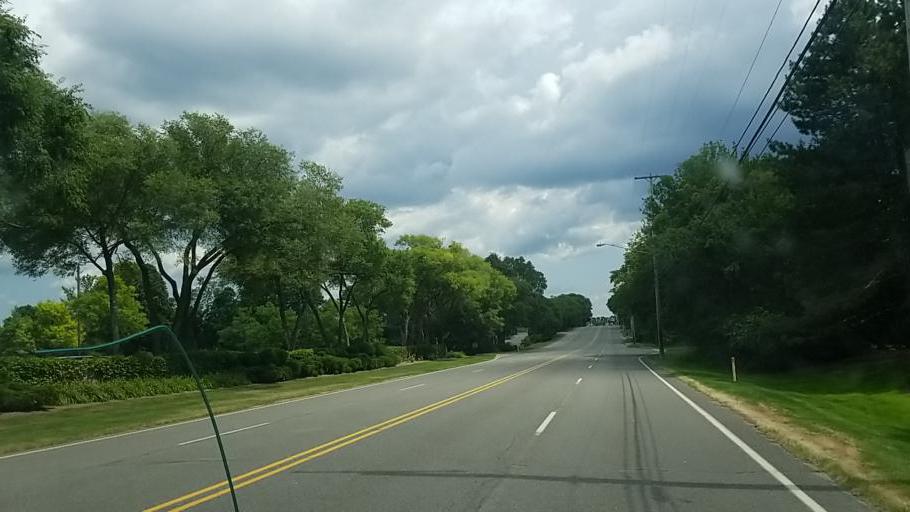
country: US
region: Michigan
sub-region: Kent County
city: East Grand Rapids
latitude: 42.9516
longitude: -85.5773
